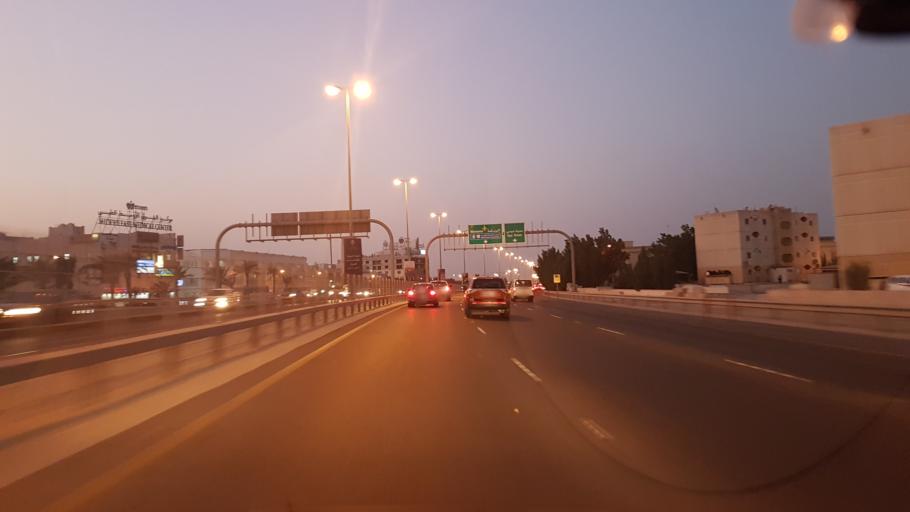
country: BH
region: Northern
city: Madinat `Isa
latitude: 26.1801
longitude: 50.5380
